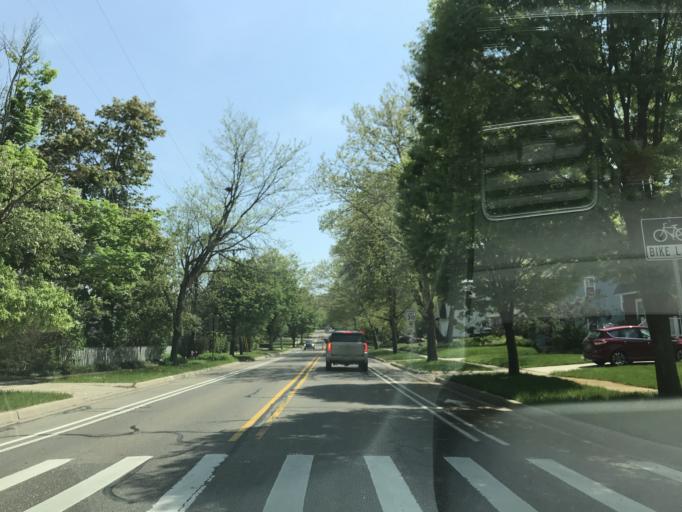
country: US
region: Michigan
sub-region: Washtenaw County
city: Ann Arbor
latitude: 42.2666
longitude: -83.7582
